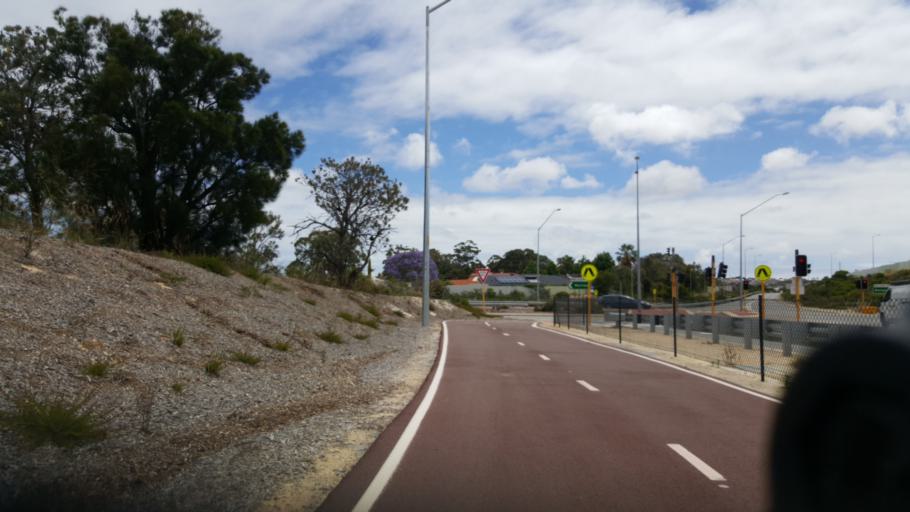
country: AU
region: Western Australia
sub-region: Bayswater
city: Embleton
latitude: -31.8682
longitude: 115.8971
